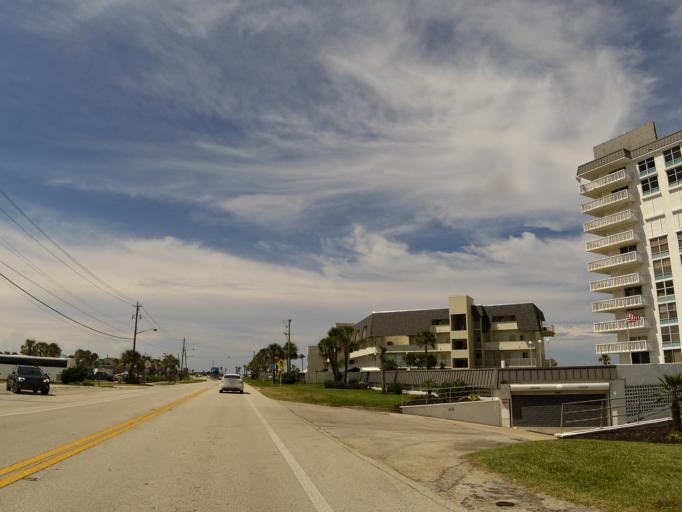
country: US
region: Florida
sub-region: Volusia County
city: Ormond-by-the-Sea
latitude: 29.3317
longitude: -81.0589
